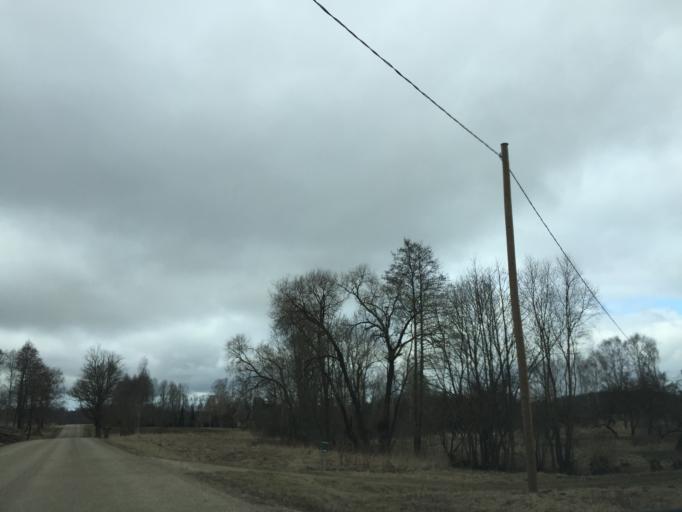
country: LV
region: Ilukste
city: Ilukste
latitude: 56.0614
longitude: 26.1605
